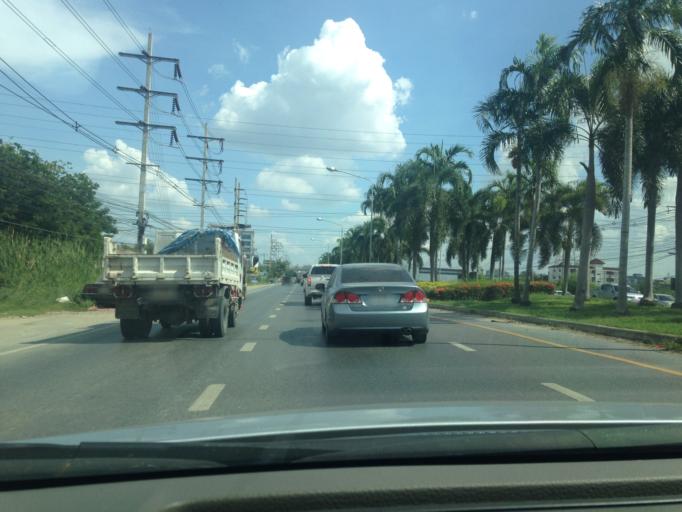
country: TH
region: Phra Nakhon Si Ayutthaya
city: Ban Bang Kadi Pathum Thani
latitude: 13.9903
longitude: 100.5826
